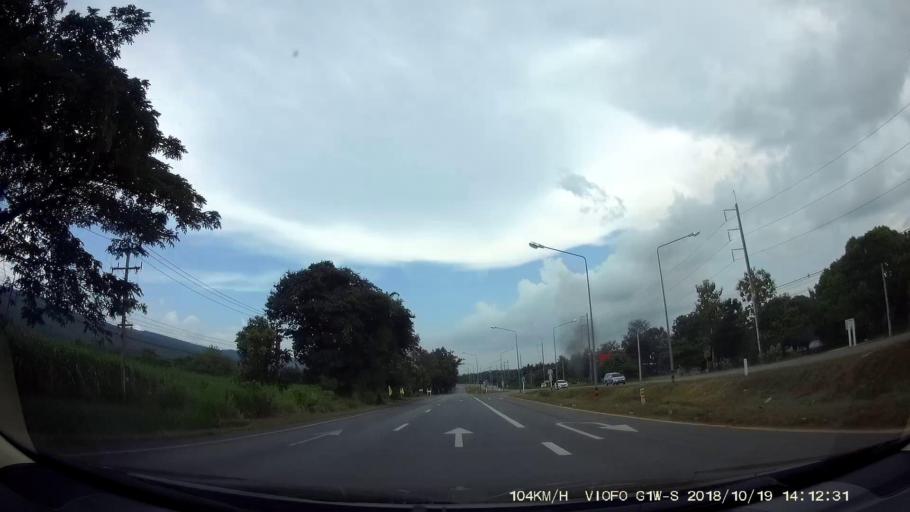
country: TH
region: Chaiyaphum
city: Khon Sawan
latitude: 15.9490
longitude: 102.1743
